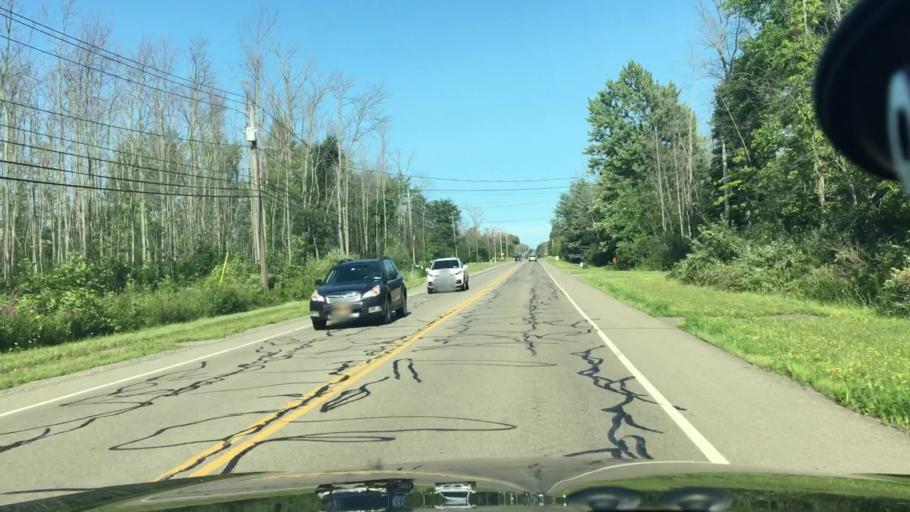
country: US
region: New York
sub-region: Erie County
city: Angola
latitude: 42.6525
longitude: -78.9952
